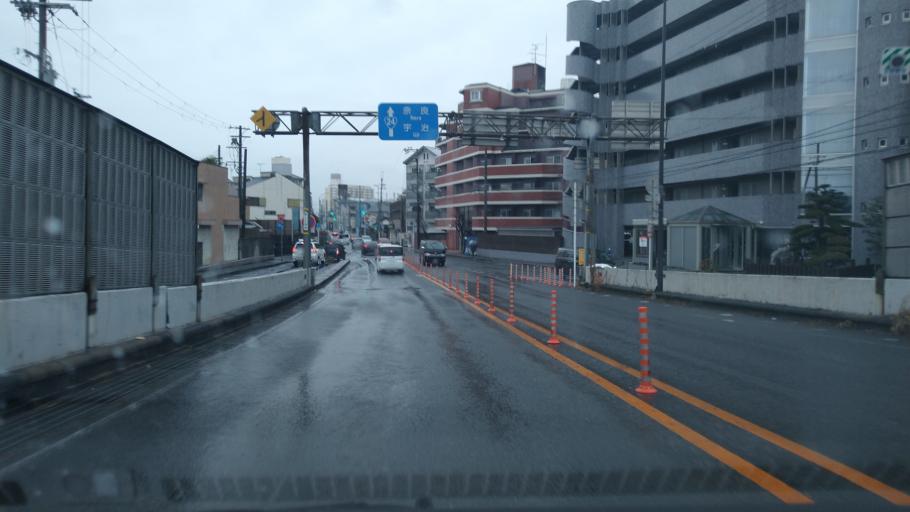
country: JP
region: Kyoto
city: Uji
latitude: 34.9241
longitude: 135.7705
